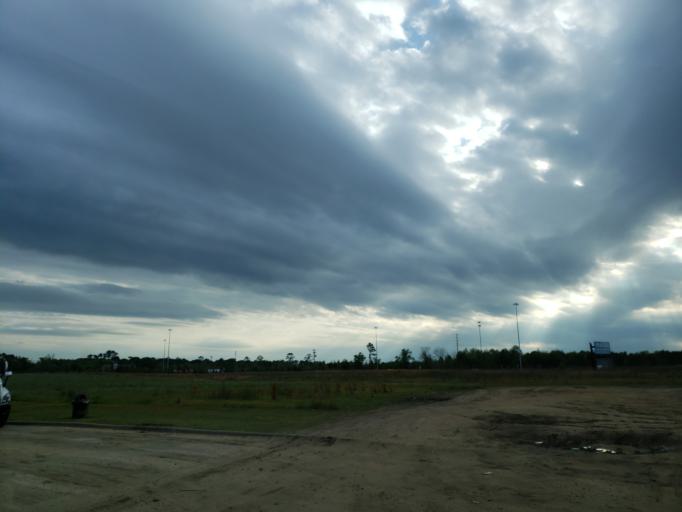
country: US
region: Georgia
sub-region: Dooly County
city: Vienna
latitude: 32.0847
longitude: -83.7601
